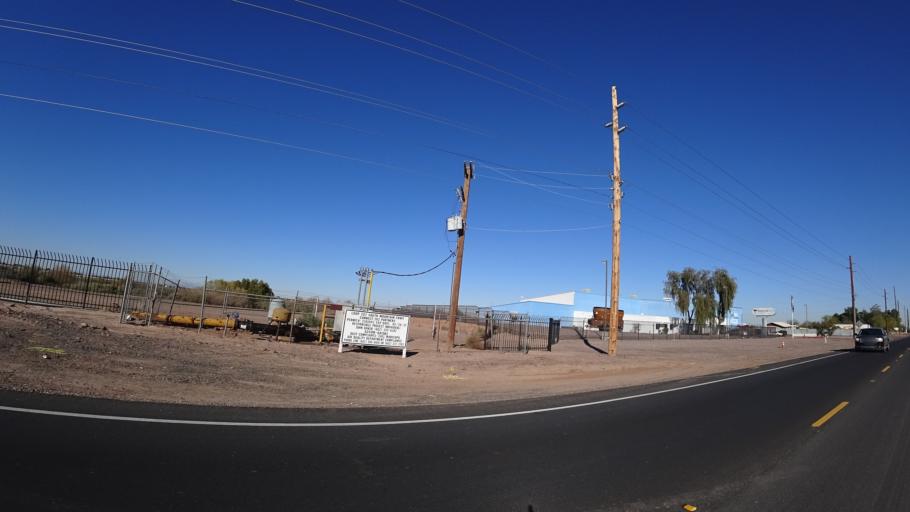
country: US
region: Arizona
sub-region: Maricopa County
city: Laveen
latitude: 33.3919
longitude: -112.1900
